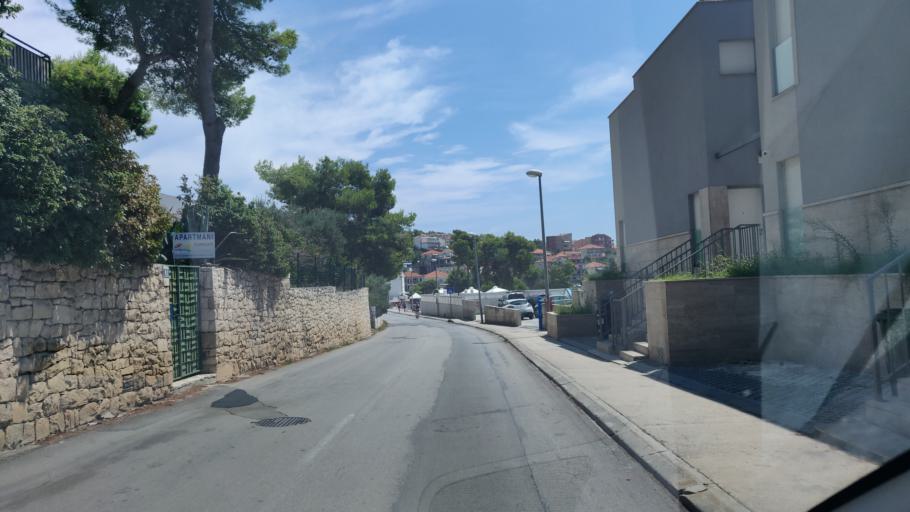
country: HR
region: Splitsko-Dalmatinska
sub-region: Grad Trogir
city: Trogir
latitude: 43.5085
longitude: 16.2570
